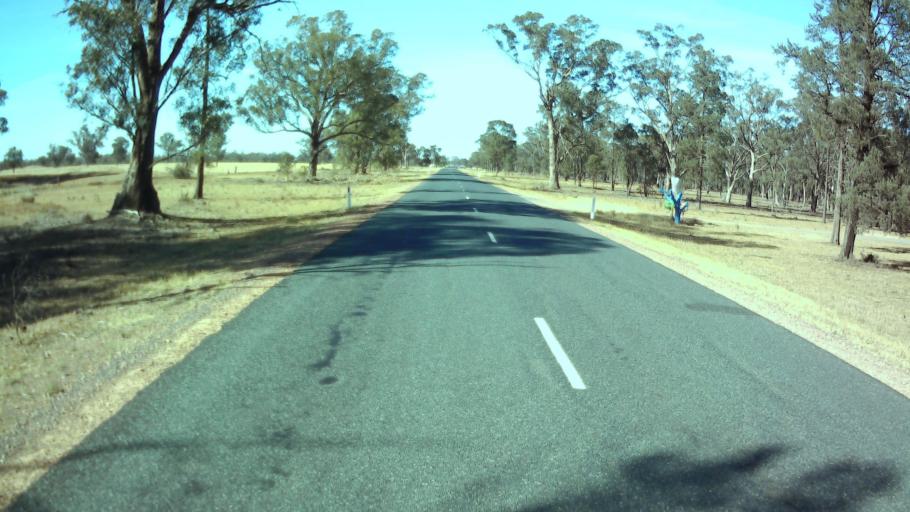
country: AU
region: New South Wales
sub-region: Weddin
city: Grenfell
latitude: -34.0919
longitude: 147.8883
